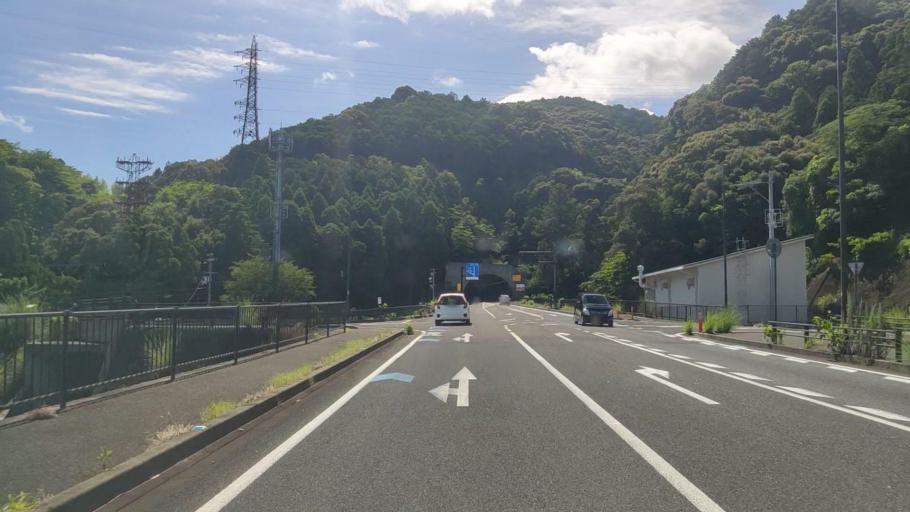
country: JP
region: Wakayama
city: Shingu
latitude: 33.7405
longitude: 135.9955
